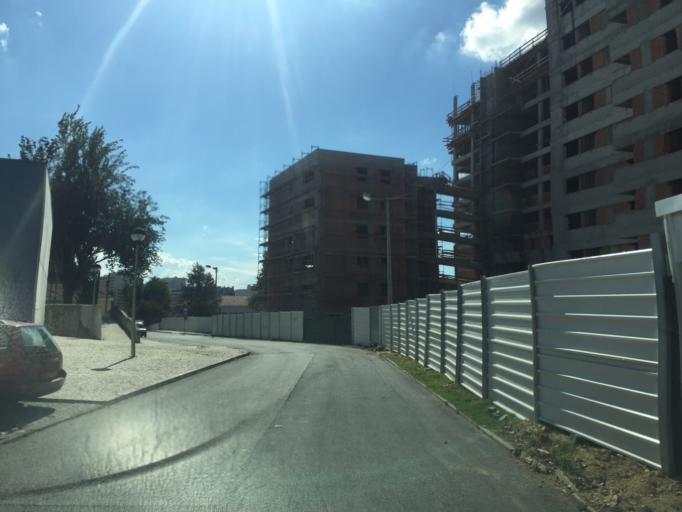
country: PT
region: Lisbon
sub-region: Odivelas
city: Olival do Basto
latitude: 38.7773
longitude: -9.1549
